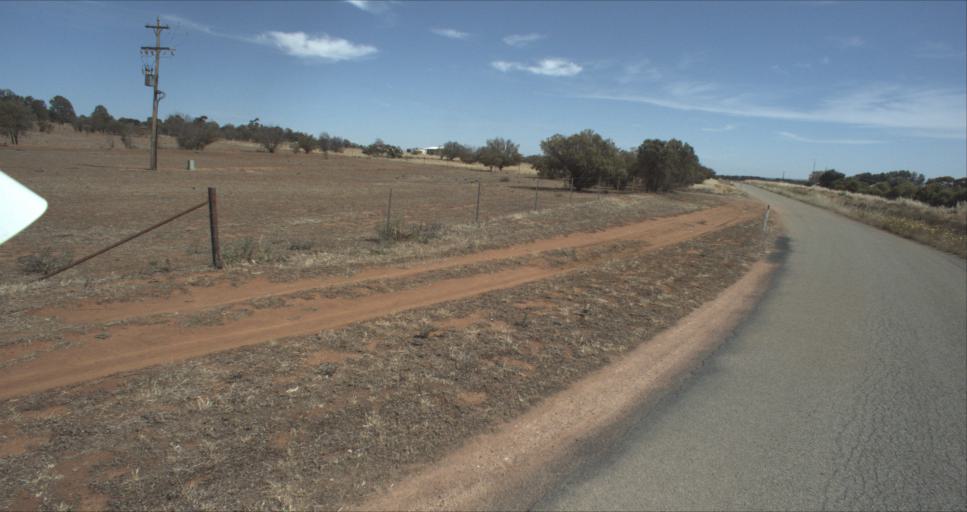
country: AU
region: New South Wales
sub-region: Leeton
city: Leeton
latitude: -34.5753
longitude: 146.4555
